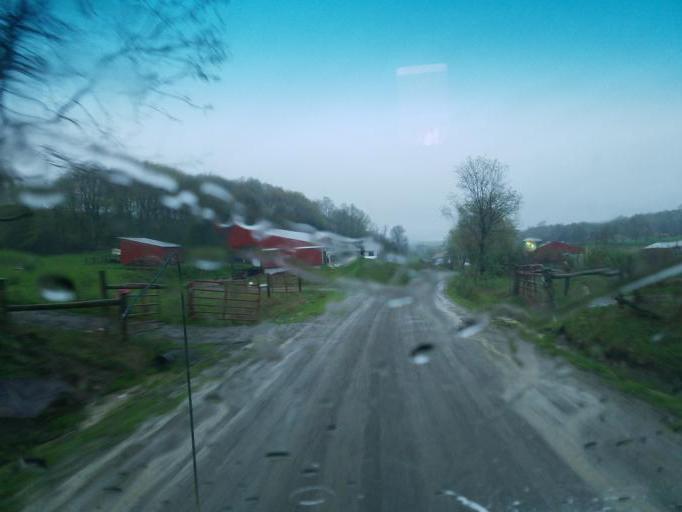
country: US
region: Pennsylvania
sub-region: Tioga County
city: Westfield
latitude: 41.9201
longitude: -77.7427
